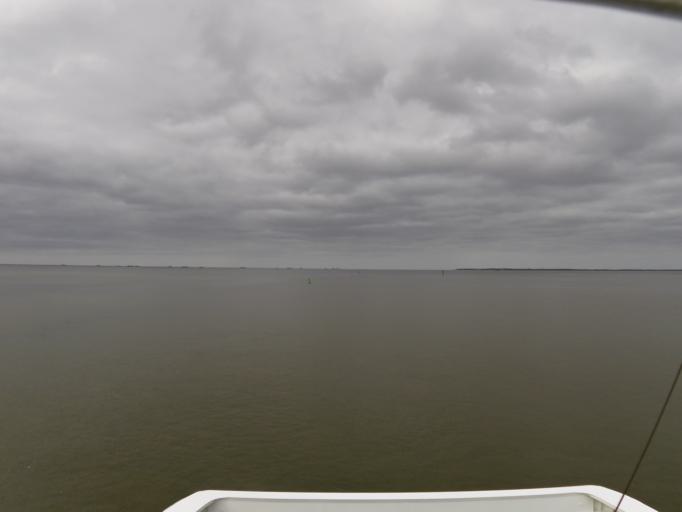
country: DE
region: Schleswig-Holstein
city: Dagebull
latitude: 54.7281
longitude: 8.6814
